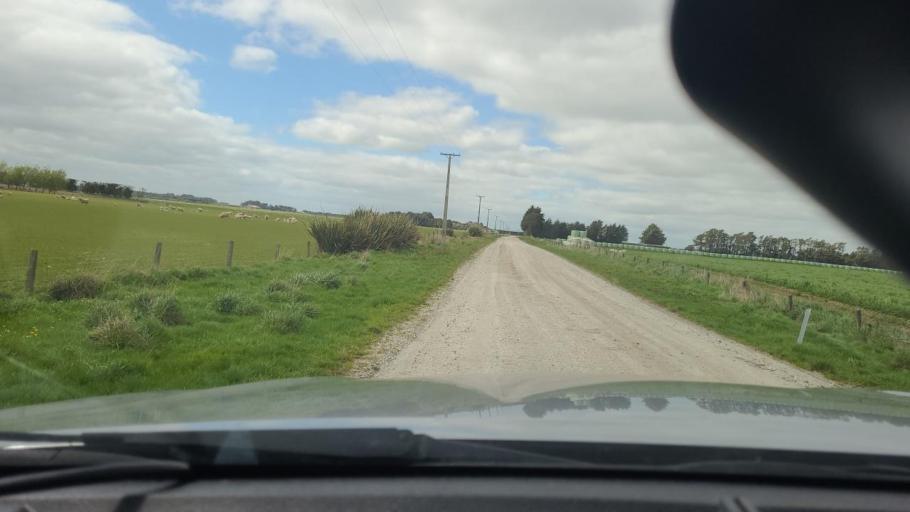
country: NZ
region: Southland
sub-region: Invercargill City
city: Invercargill
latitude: -46.4744
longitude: 168.5065
